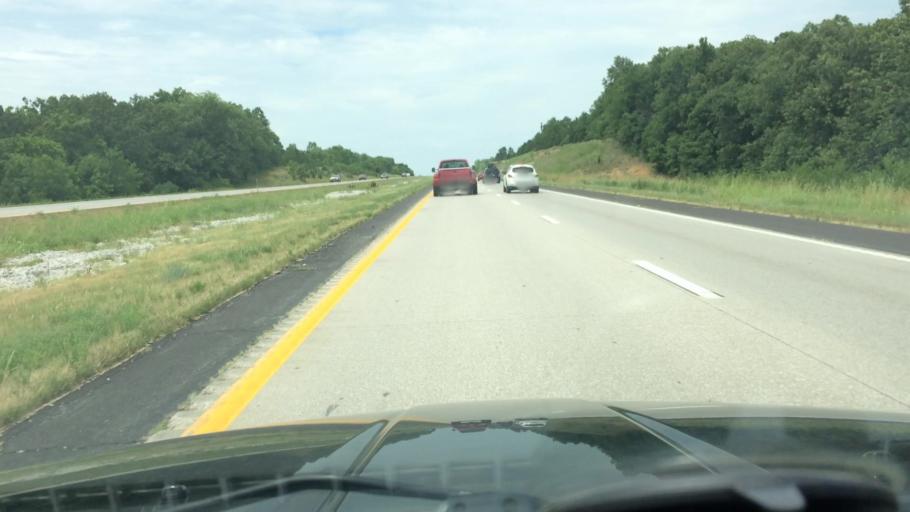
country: US
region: Missouri
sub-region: Greene County
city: Willard
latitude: 37.4375
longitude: -93.3555
